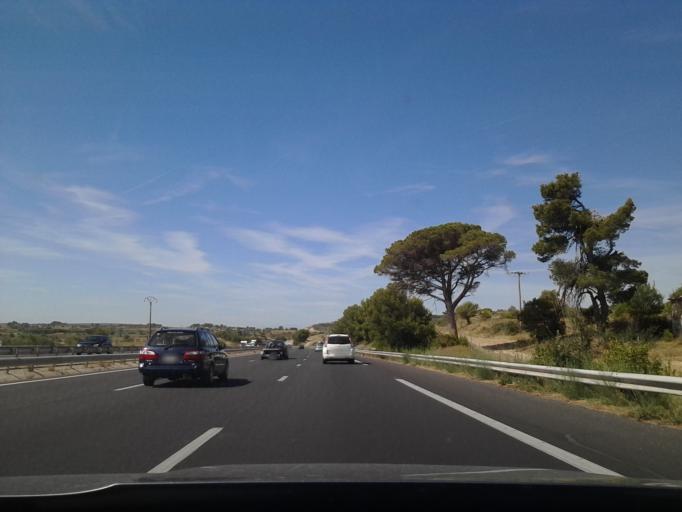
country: FR
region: Languedoc-Roussillon
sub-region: Departement de l'Herault
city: Lespignan
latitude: 43.2915
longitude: 3.1937
